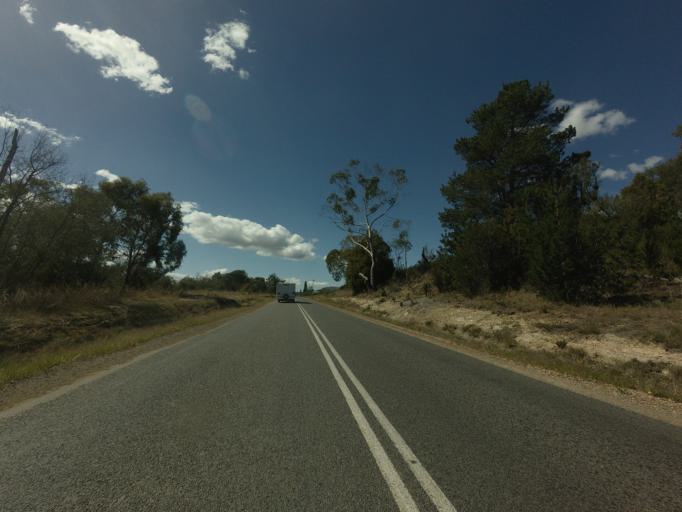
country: AU
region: Tasmania
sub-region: Break O'Day
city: St Helens
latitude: -41.6448
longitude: 147.9608
